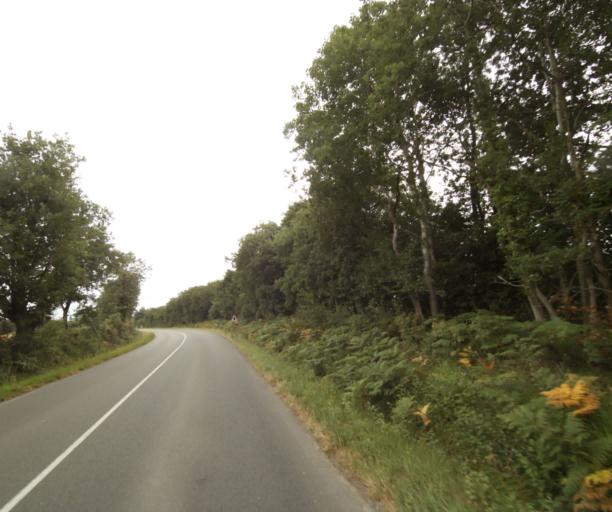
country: FR
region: Pays de la Loire
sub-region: Departement de la Vendee
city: Chateau-d'Olonne
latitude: 46.4944
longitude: -1.7005
